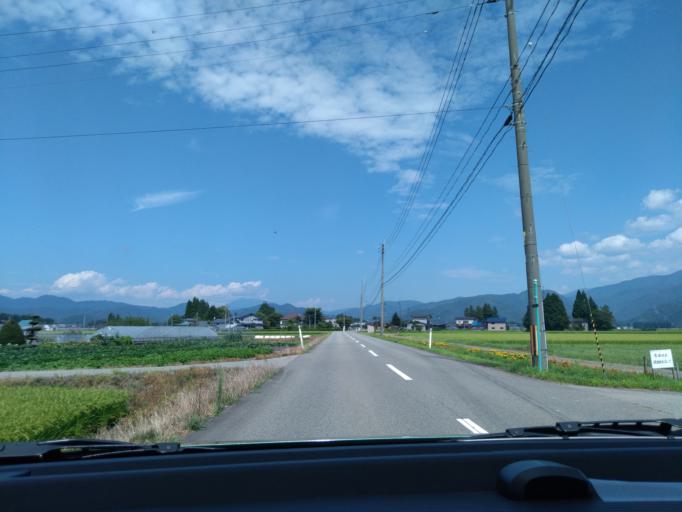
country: JP
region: Akita
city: Kakunodatemachi
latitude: 39.6037
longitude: 140.5883
